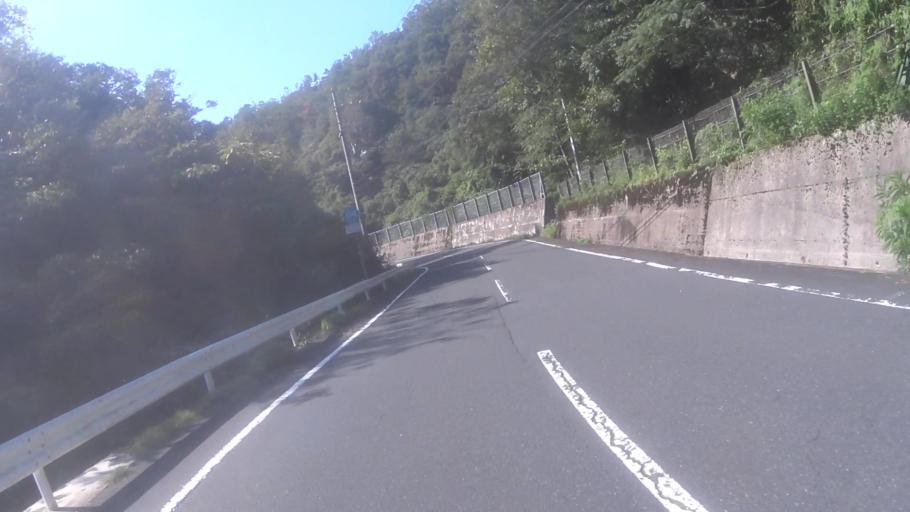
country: JP
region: Kyoto
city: Miyazu
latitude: 35.6919
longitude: 135.1317
